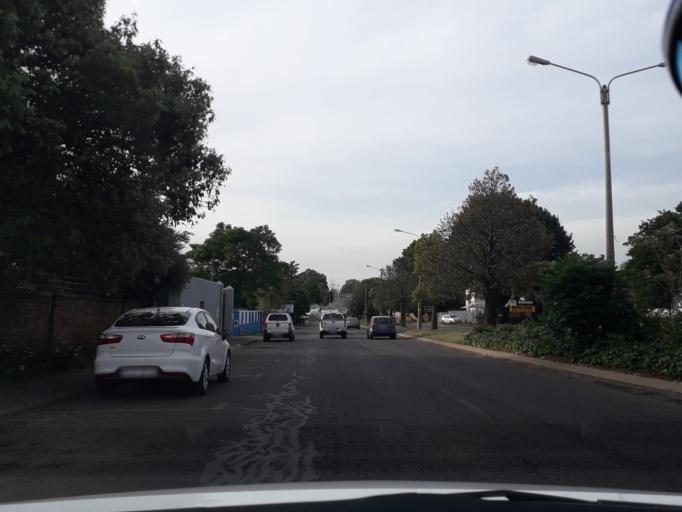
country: ZA
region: Gauteng
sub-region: City of Johannesburg Metropolitan Municipality
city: Modderfontein
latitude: -26.1523
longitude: 28.1519
